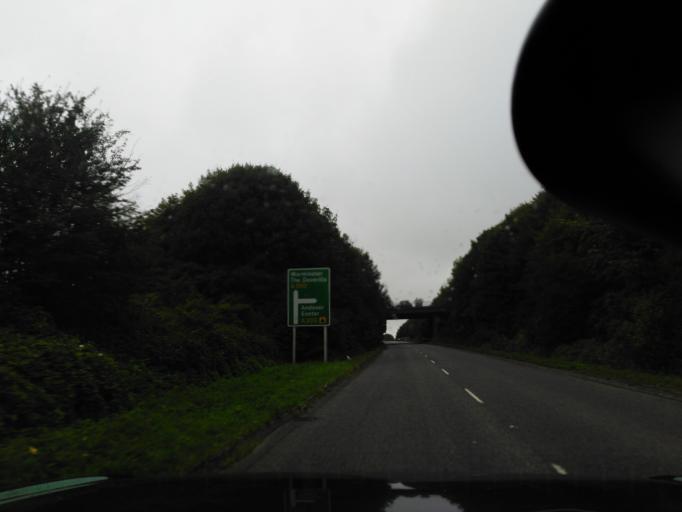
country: GB
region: England
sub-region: Wiltshire
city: Chicklade
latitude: 51.1041
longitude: -2.1651
